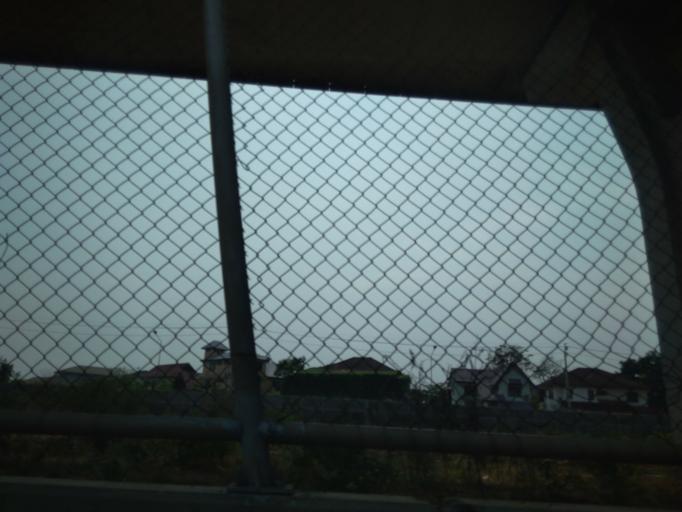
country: TH
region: Bangkok
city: Taling Chan
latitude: 13.7929
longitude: 100.4360
